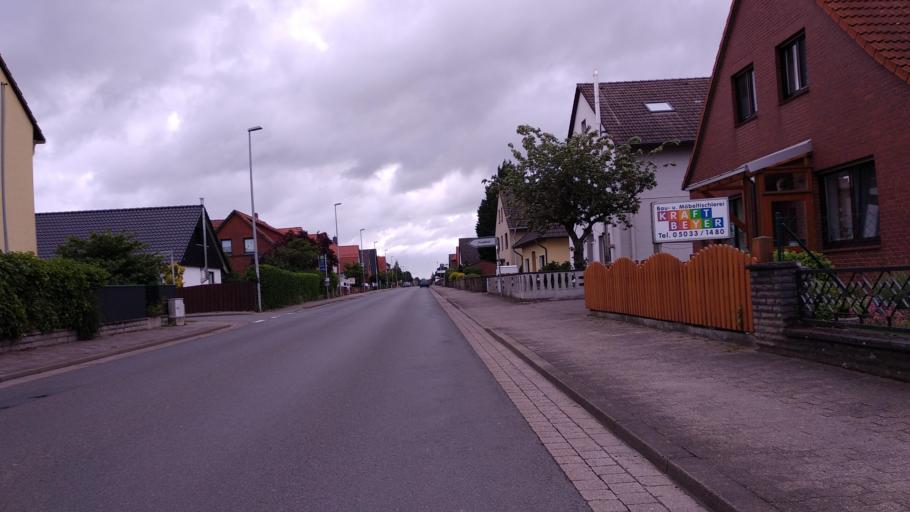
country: DE
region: Lower Saxony
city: Hagenburg
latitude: 52.4540
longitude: 9.3625
